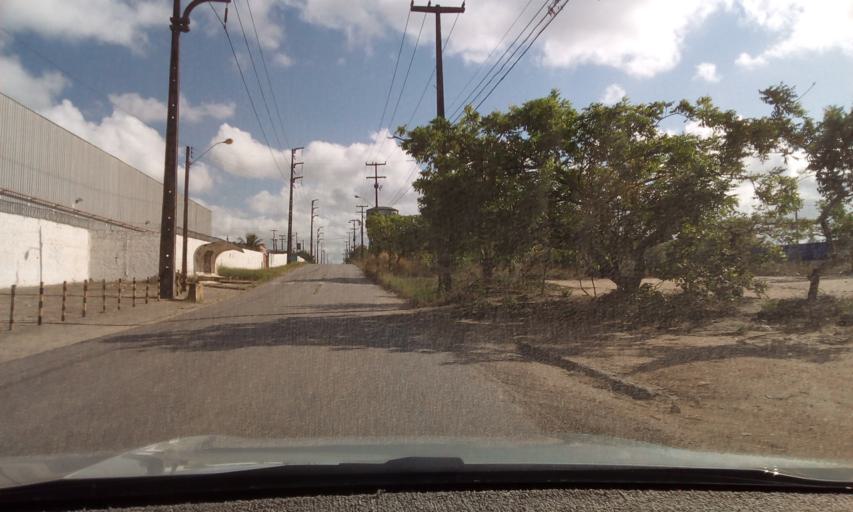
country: BR
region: Paraiba
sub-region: Bayeux
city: Bayeux
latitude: -7.1740
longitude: -34.9072
